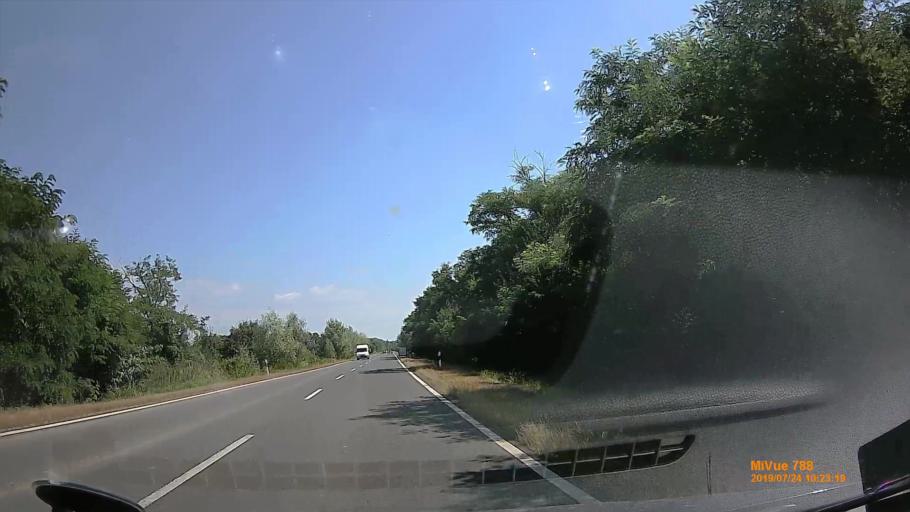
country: HU
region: Szabolcs-Szatmar-Bereg
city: Vasarosnameny
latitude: 48.1472
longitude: 22.3655
